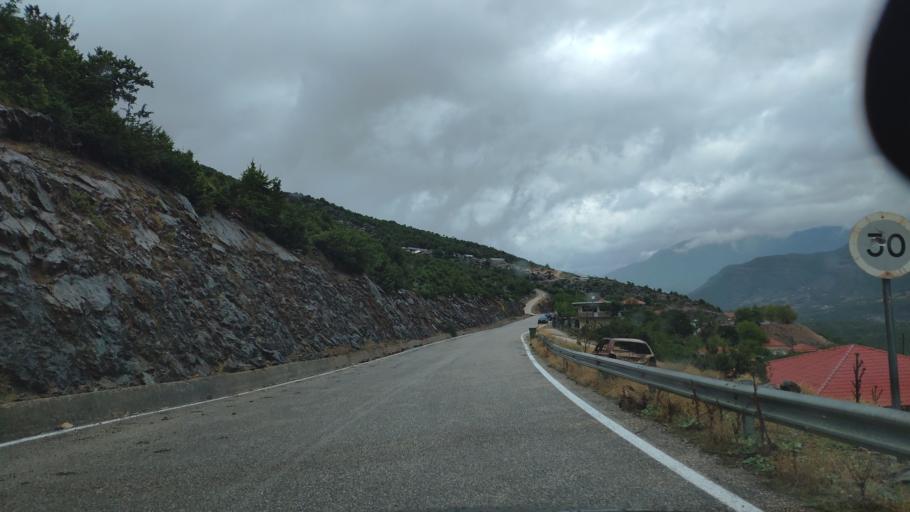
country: GR
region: Thessaly
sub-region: Nomos Kardhitsas
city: Anthiro
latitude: 39.1067
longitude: 21.4080
